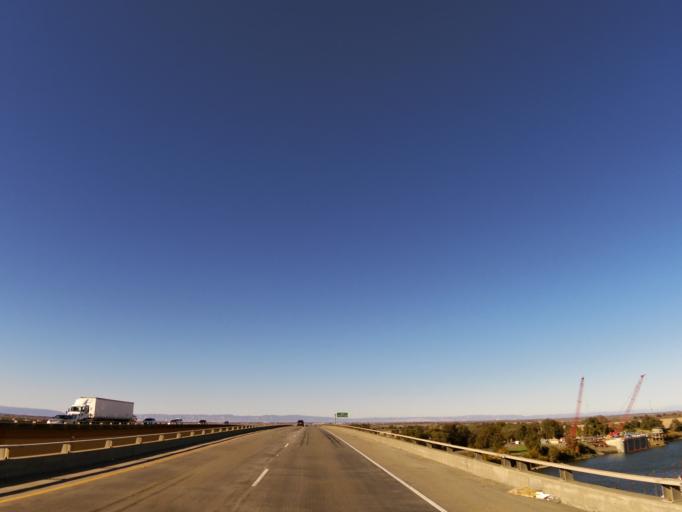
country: US
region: California
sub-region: Yolo County
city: West Sacramento
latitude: 38.6734
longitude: -121.6253
